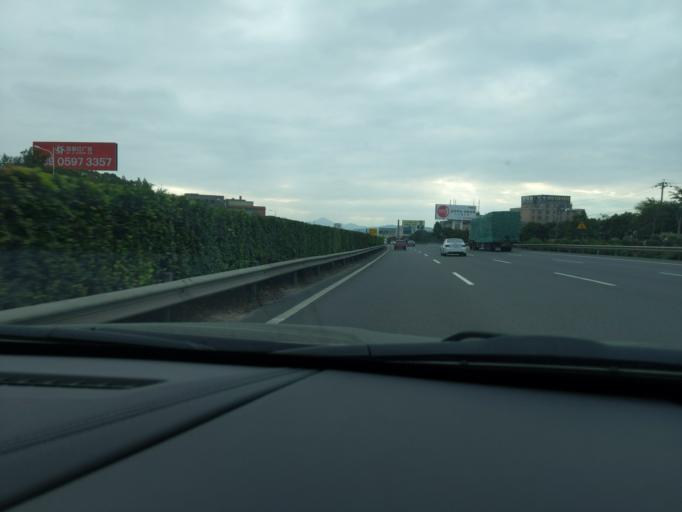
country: CN
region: Fujian
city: Neikeng
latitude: 24.7473
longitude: 118.4315
